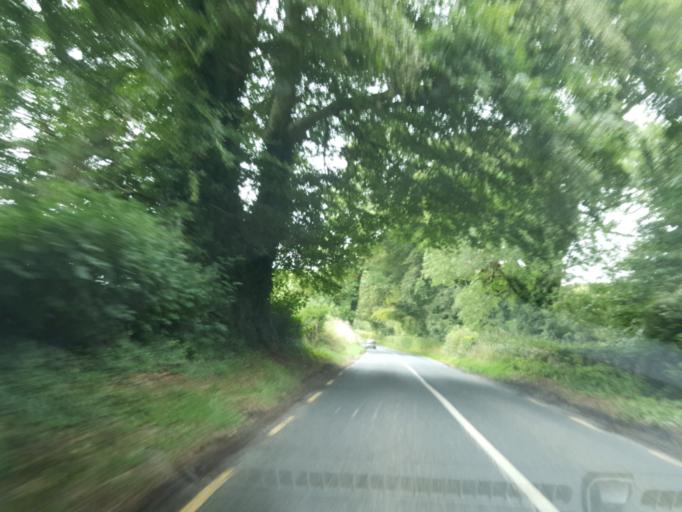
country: IE
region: Leinster
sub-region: Kildare
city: Kilcullen
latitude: 53.1219
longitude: -6.7297
